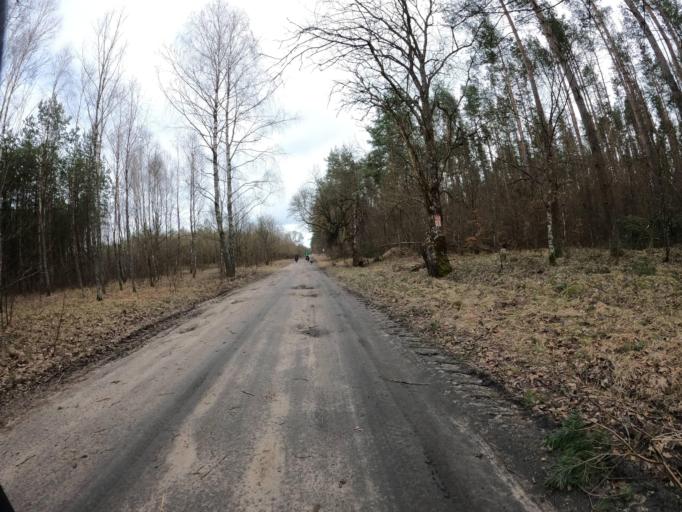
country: PL
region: Greater Poland Voivodeship
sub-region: Powiat zlotowski
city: Sypniewo
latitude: 53.4587
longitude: 16.5181
